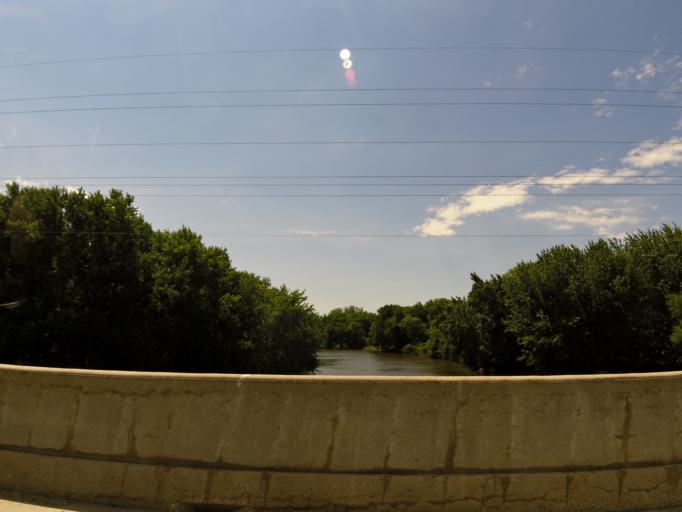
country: US
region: Iowa
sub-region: Bremer County
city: Tripoli
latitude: 42.7147
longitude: -92.1727
